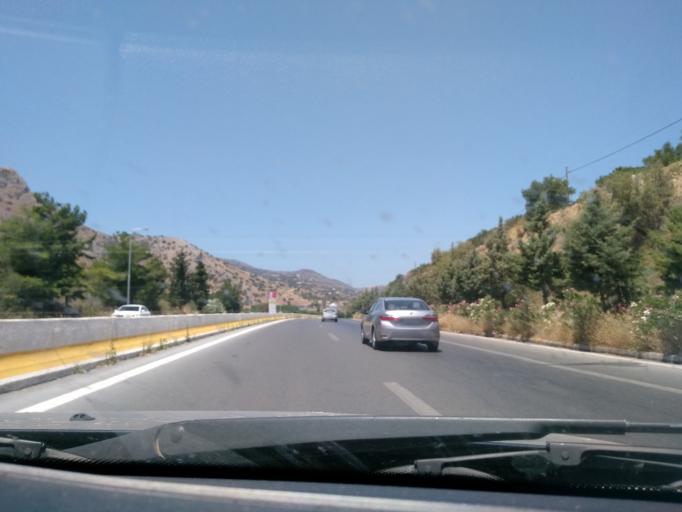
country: GR
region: Crete
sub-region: Nomos Irakleiou
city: Gazi
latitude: 35.3271
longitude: 25.0550
